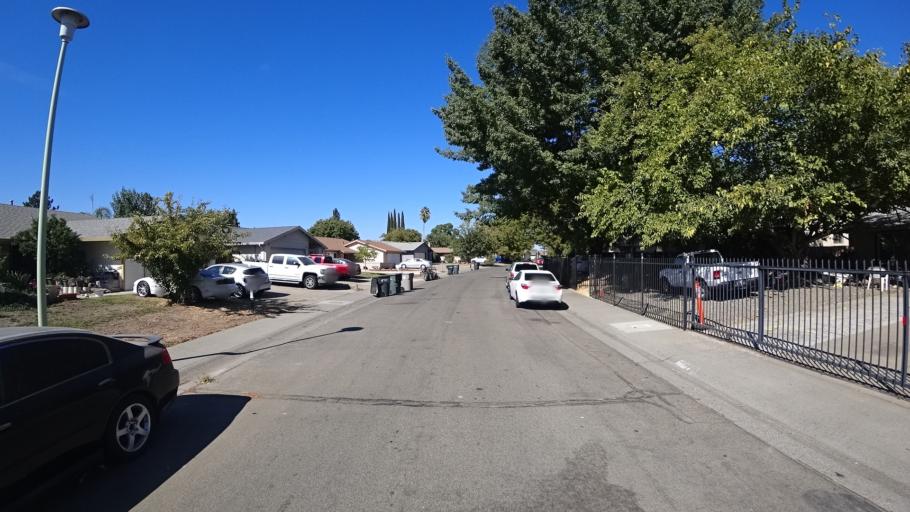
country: US
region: California
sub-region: Sacramento County
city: Florin
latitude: 38.4771
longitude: -121.4335
